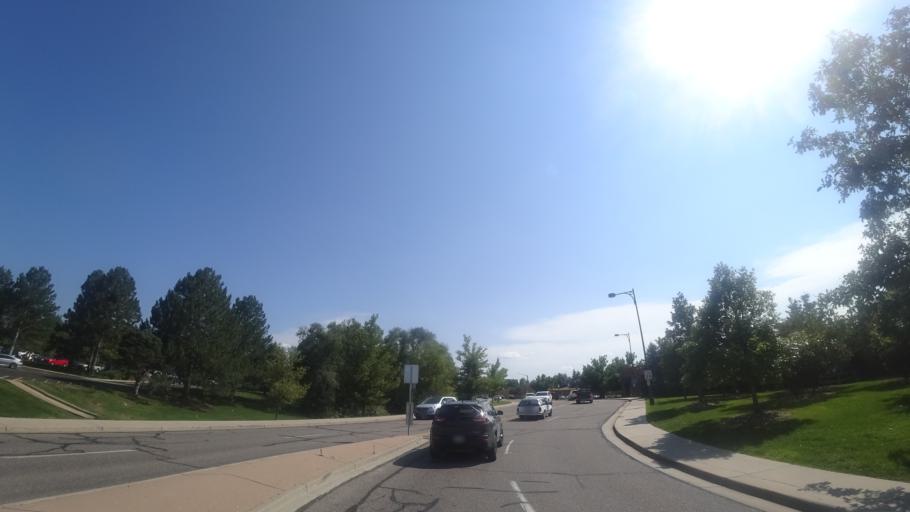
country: US
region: Colorado
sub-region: Arapahoe County
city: Littleton
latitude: 39.6201
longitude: -105.0159
